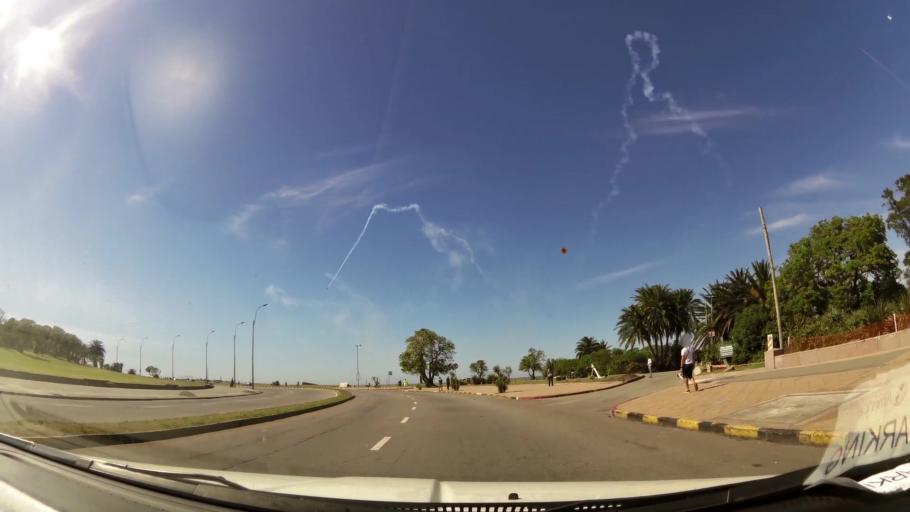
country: UY
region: Montevideo
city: Montevideo
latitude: -34.9239
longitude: -56.1711
